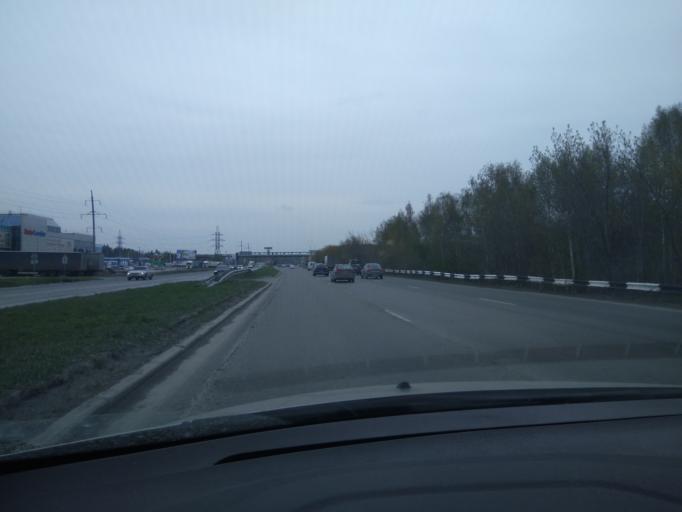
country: RU
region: Sverdlovsk
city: Istok
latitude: 56.8234
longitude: 60.6995
